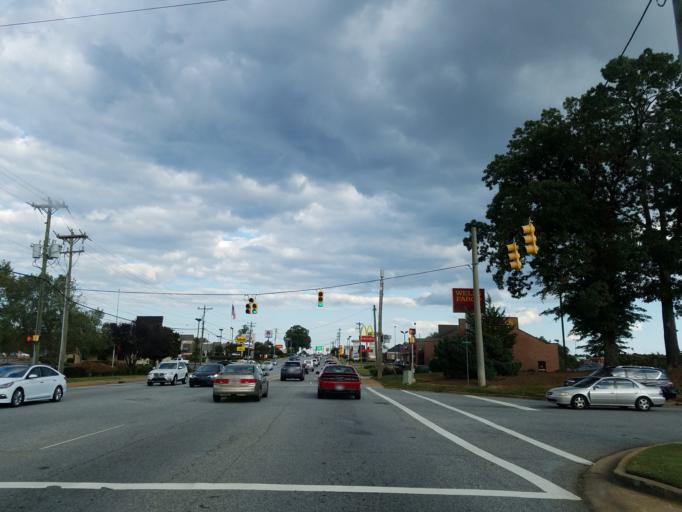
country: US
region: South Carolina
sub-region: Greenville County
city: Taylors
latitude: 34.8604
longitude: -82.2707
